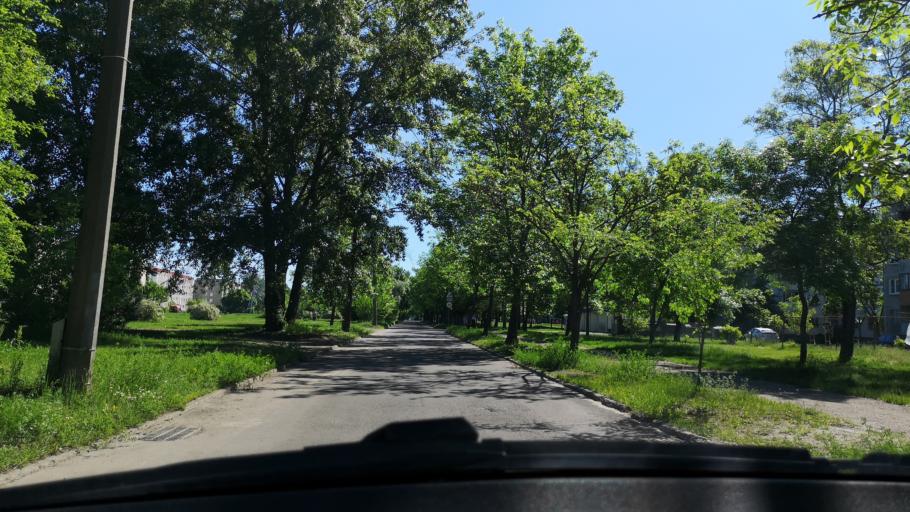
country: BY
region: Brest
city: Brest
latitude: 52.1025
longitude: 23.7520
